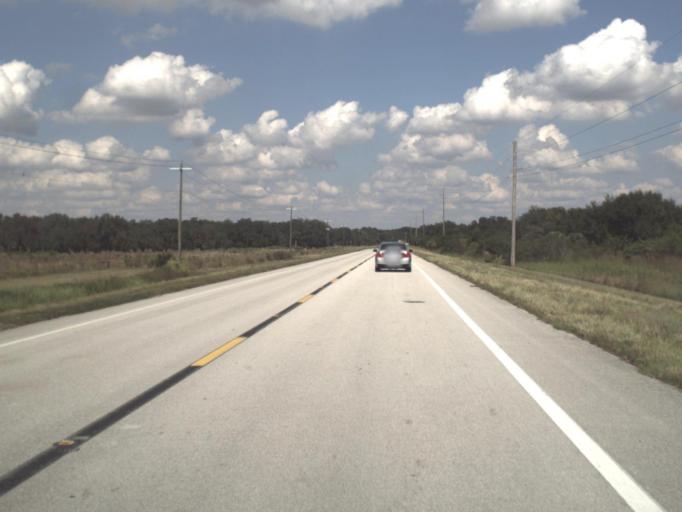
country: US
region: Florida
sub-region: Okeechobee County
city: Okeechobee
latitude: 27.3795
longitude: -81.0420
